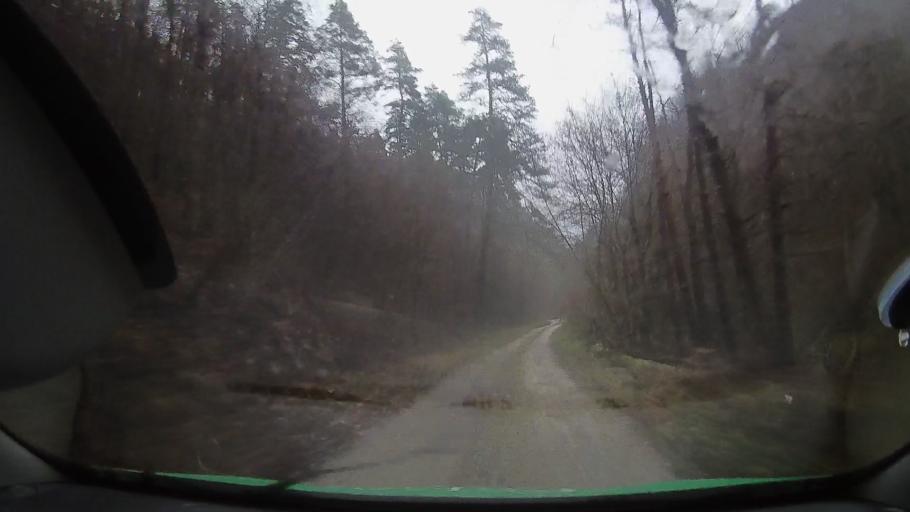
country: RO
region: Alba
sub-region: Comuna Avram Iancu
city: Avram Iancu
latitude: 46.3075
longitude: 22.7692
